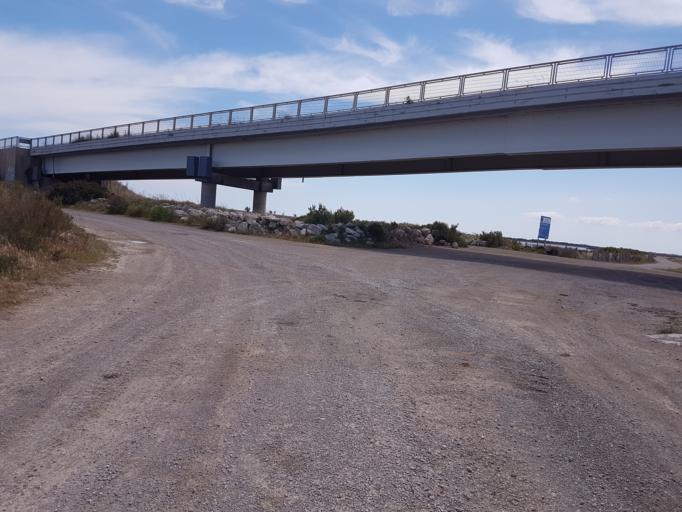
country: FR
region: Languedoc-Roussillon
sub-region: Departement de l'Herault
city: Vic-la-Gardiole
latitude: 43.4645
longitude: 3.8182
